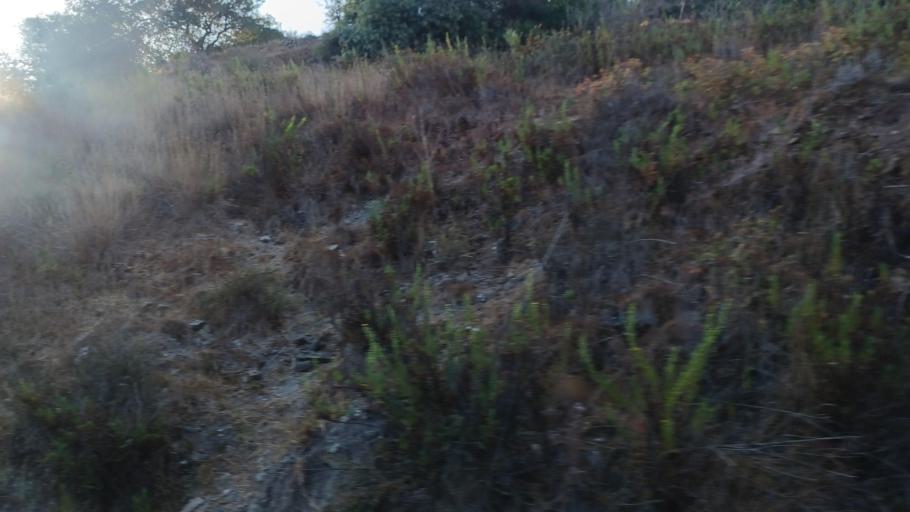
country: CY
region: Pafos
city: Polis
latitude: 34.9703
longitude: 32.4185
